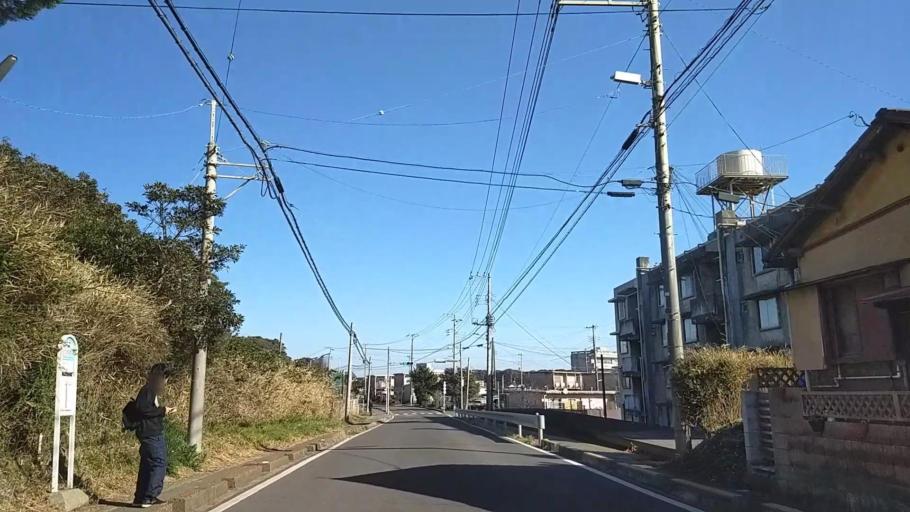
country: JP
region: Chiba
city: Hasaki
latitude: 35.7007
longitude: 140.8575
